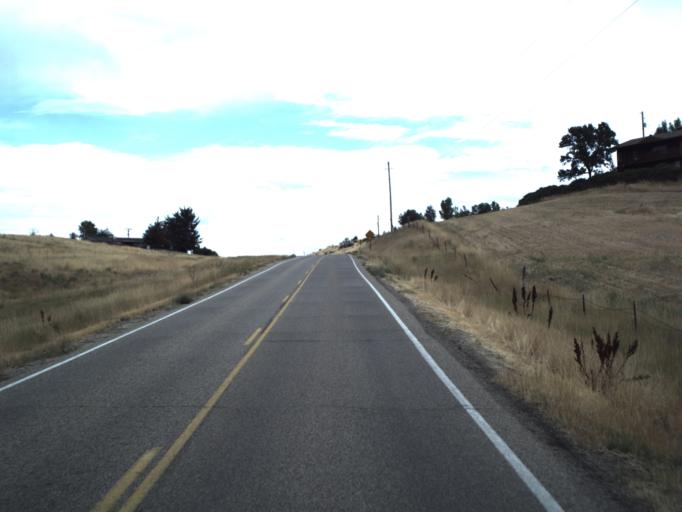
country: US
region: Utah
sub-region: Morgan County
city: Morgan
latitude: 40.9894
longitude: -111.6796
